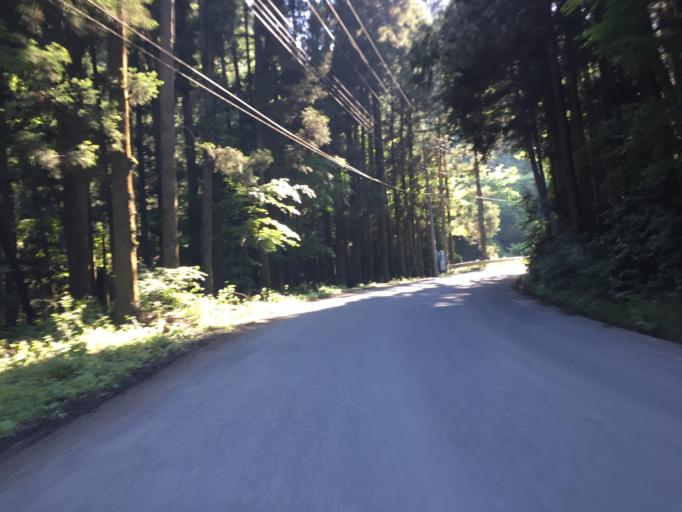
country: JP
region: Ibaraki
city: Kitaibaraki
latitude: 36.8654
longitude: 140.7107
